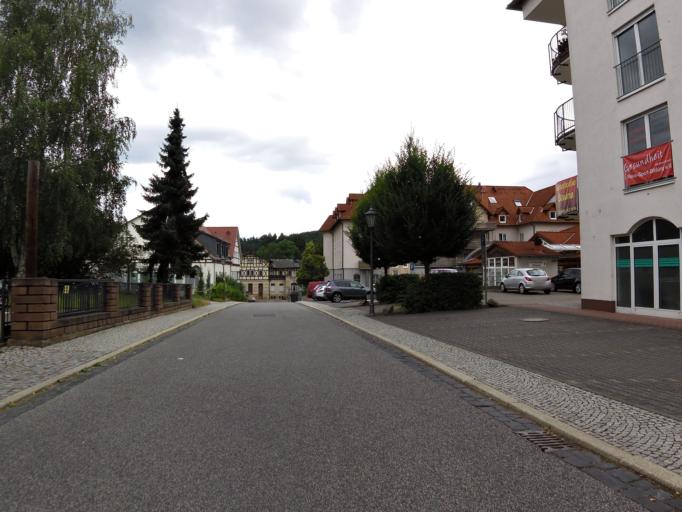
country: DE
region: Thuringia
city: Bad Salzungen
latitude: 50.8136
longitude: 10.2312
